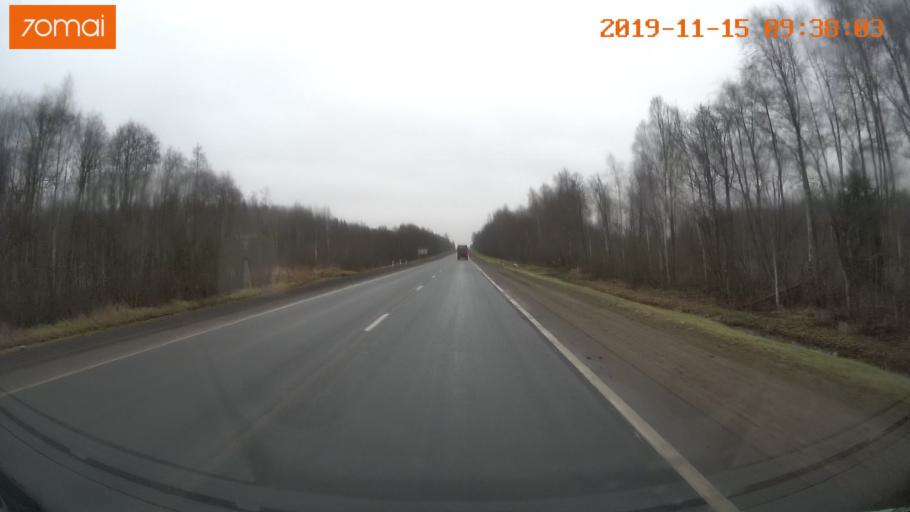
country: RU
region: Vologda
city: Sheksna
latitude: 59.2355
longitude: 38.4481
